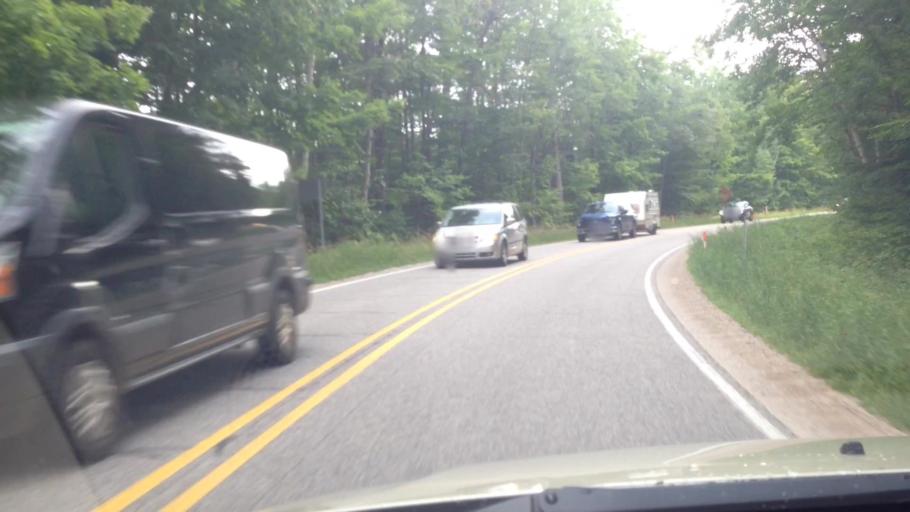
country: US
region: Michigan
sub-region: Mackinac County
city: Saint Ignace
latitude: 46.0458
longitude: -85.1125
